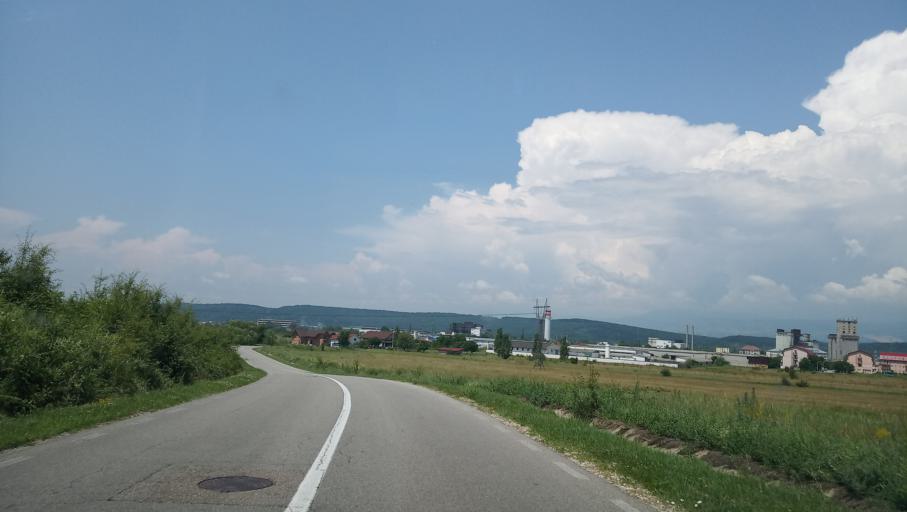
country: RO
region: Gorj
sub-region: Comuna Turcinesti
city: Turcinesti
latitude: 45.0655
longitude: 23.3179
